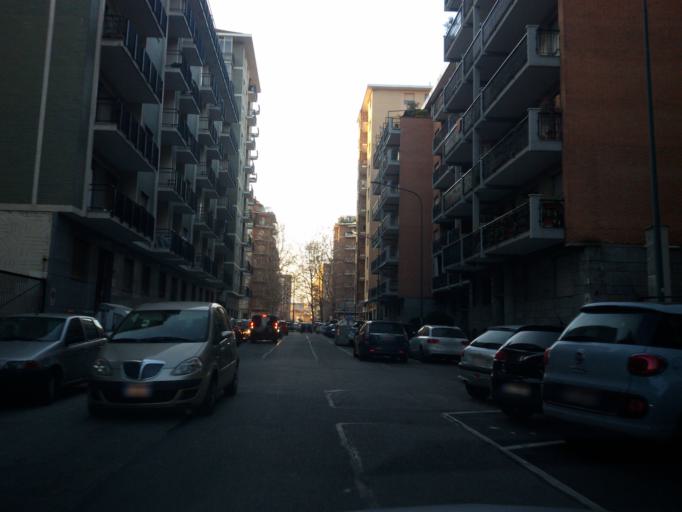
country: IT
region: Piedmont
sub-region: Provincia di Torino
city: Lesna
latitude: 45.0470
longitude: 7.6358
